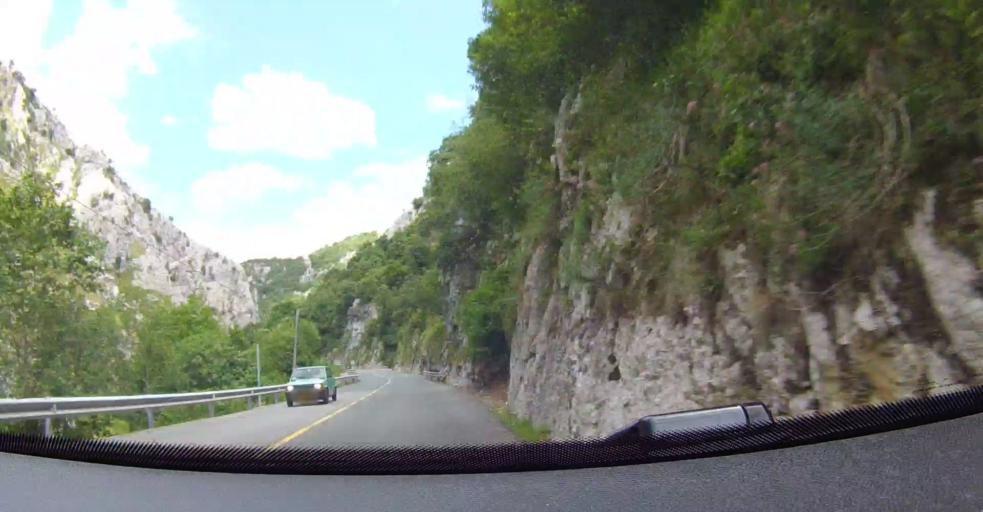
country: ES
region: Cantabria
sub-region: Provincia de Cantabria
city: Tresviso
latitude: 43.2990
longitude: -4.6069
